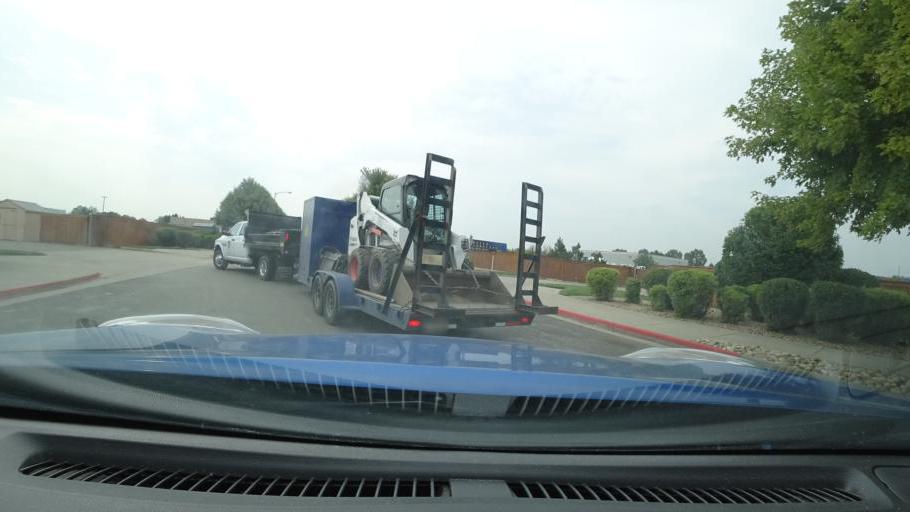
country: US
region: Colorado
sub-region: Adams County
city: Aurora
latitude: 39.7501
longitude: -104.7825
